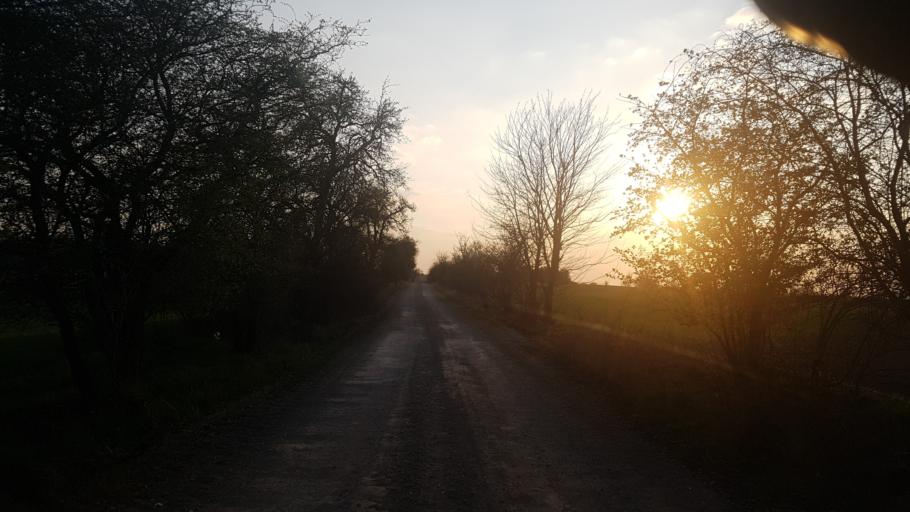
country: DE
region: Brandenburg
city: Gramzow
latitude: 53.2141
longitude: 13.9532
